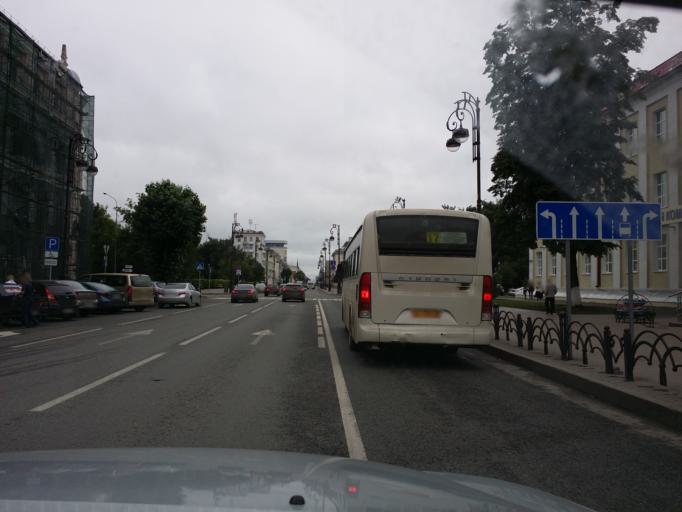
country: RU
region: Tjumen
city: Tyumen
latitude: 57.1519
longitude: 65.5429
